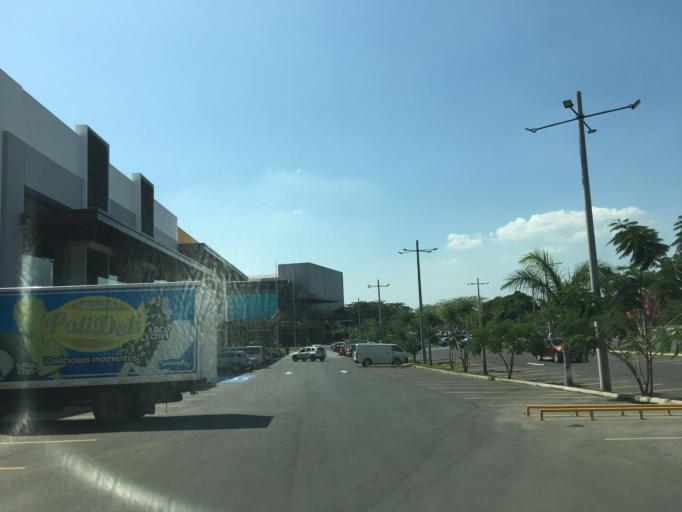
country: GT
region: Escuintla
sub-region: Municipio de Escuintla
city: Escuintla
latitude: 14.2954
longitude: -90.7982
